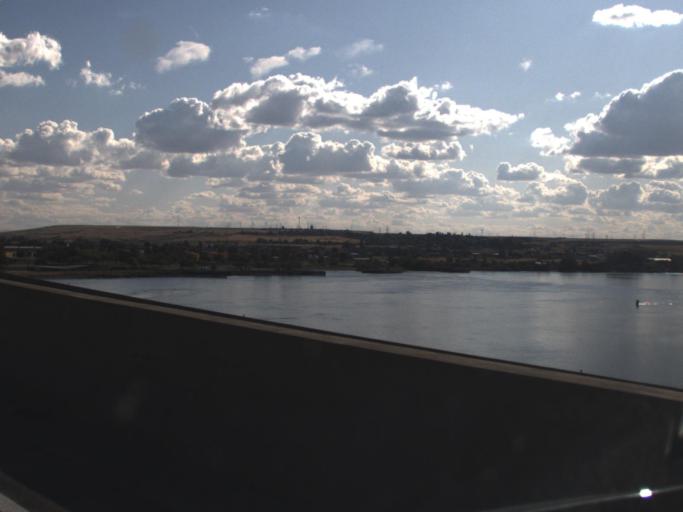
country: US
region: Oregon
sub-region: Umatilla County
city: Umatilla
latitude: 45.9339
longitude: -119.3298
